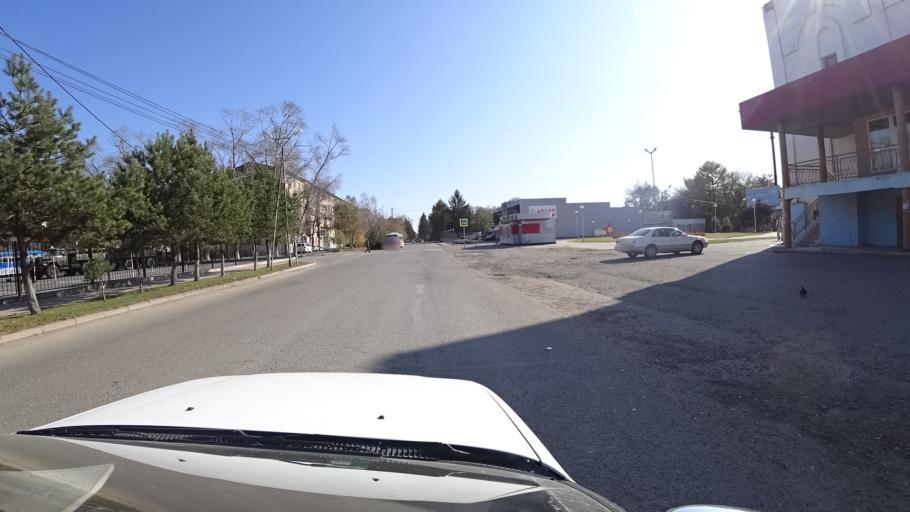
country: RU
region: Primorskiy
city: Dal'nerechensk
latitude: 45.9338
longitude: 133.7290
